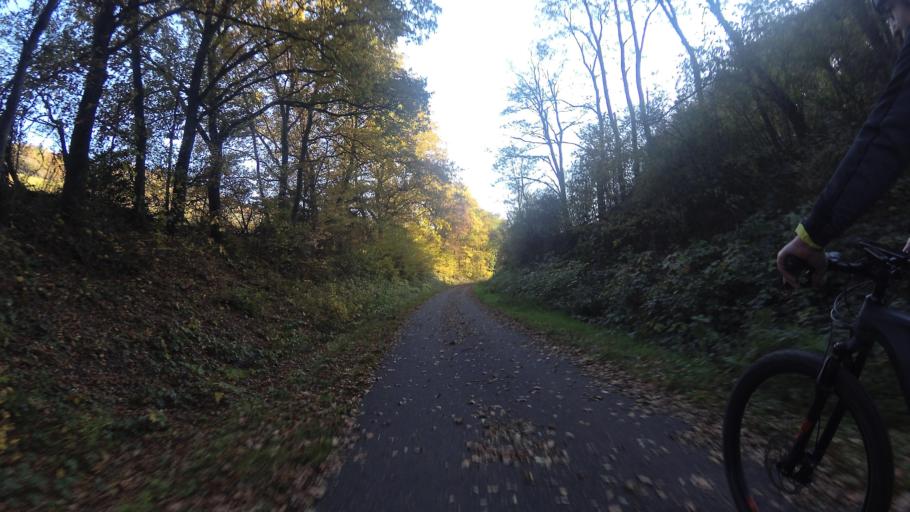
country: DE
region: Rheinland-Pfalz
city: Waldrach
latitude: 49.7392
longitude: 6.7445
